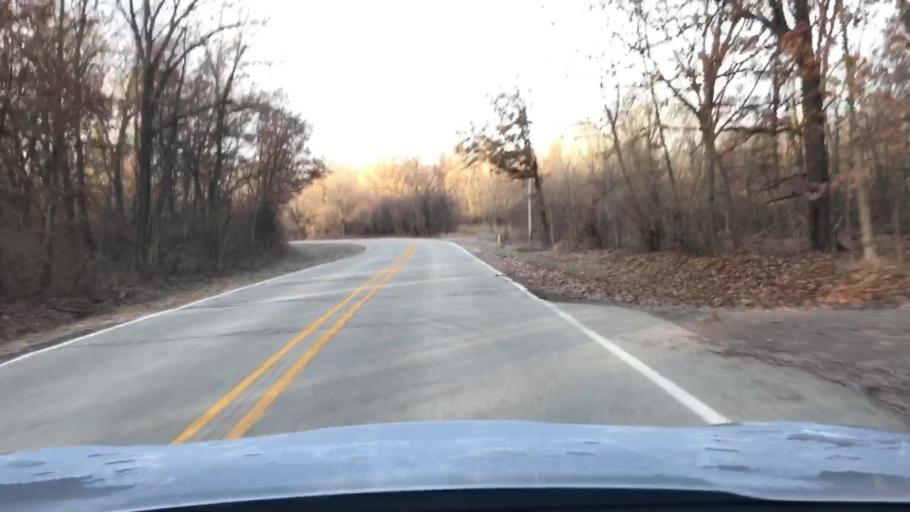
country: US
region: Illinois
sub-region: McLean County
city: Hudson
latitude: 40.6419
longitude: -88.9160
